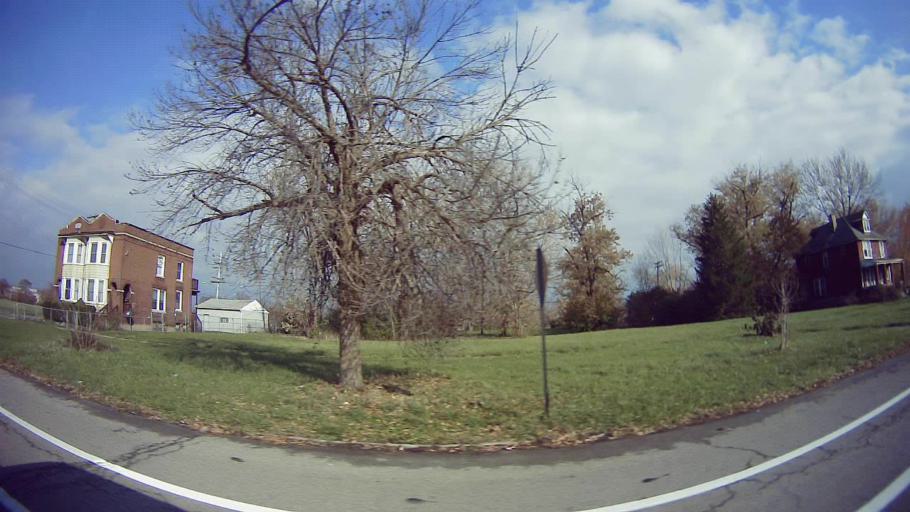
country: US
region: Michigan
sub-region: Wayne County
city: Detroit
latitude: 42.3387
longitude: -83.1035
